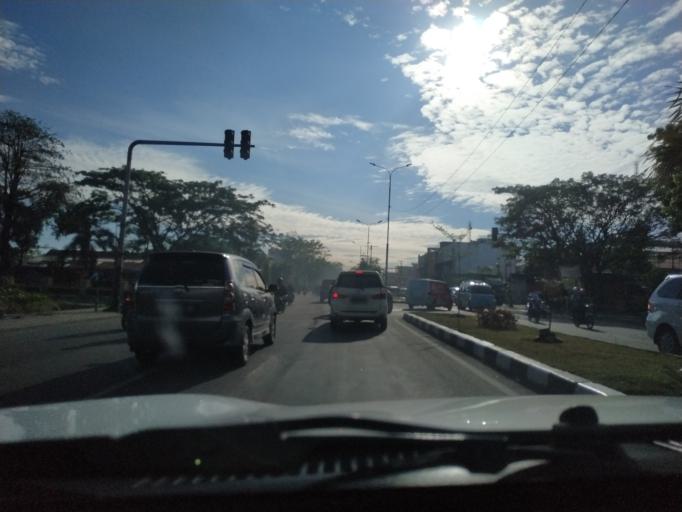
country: ID
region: North Sumatra
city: Medan
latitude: 3.5974
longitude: 98.7242
